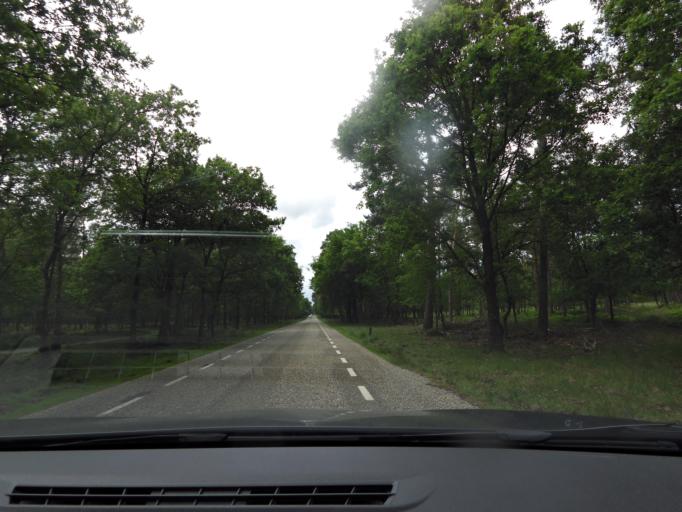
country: NL
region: Gelderland
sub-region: Gemeente Apeldoorn
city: Uddel
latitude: 52.2527
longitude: 5.8056
